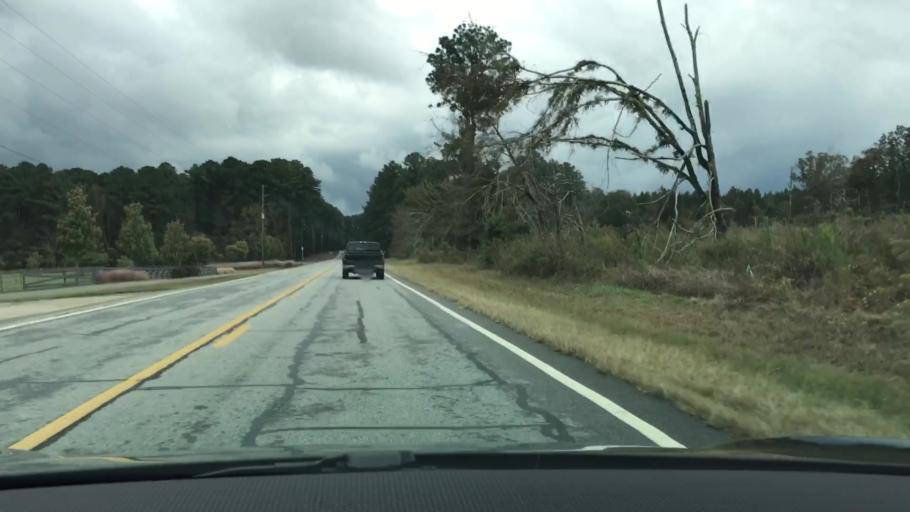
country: US
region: Georgia
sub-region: Oconee County
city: Watkinsville
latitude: 33.7864
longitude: -83.3168
